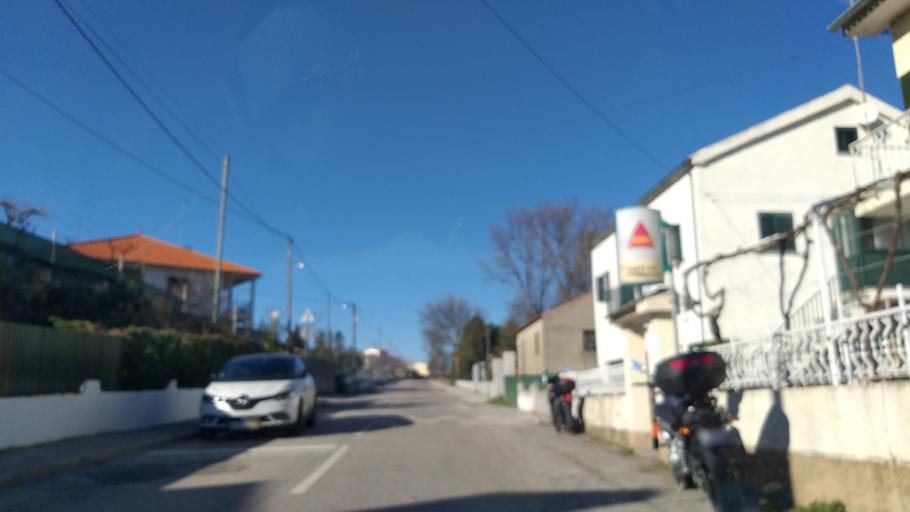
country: PT
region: Guarda
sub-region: Celorico da Beira
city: Celorico da Beira
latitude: 40.6073
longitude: -7.3626
